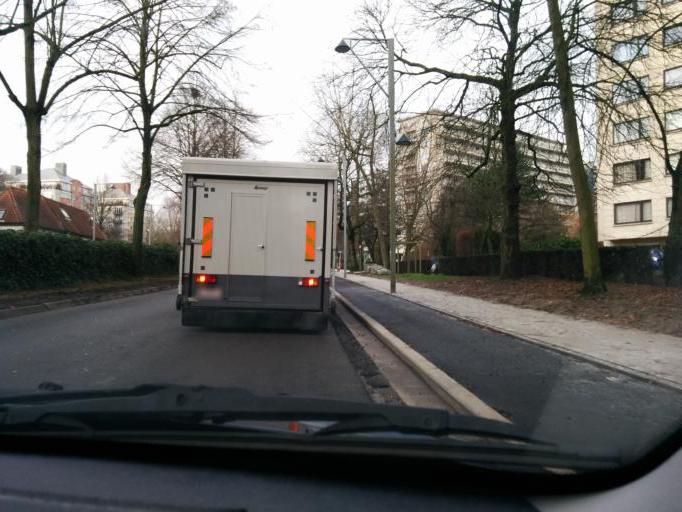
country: BE
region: Flanders
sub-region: Provincie Vlaams-Brabant
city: Wemmel
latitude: 50.8887
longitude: 4.3162
